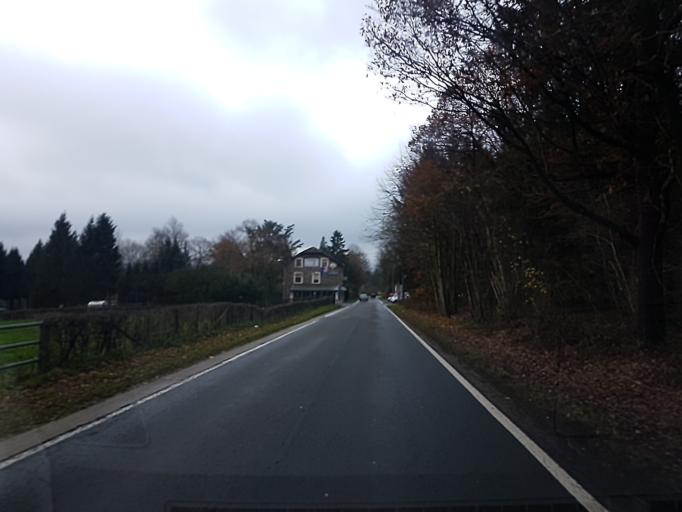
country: BE
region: Wallonia
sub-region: Province de Liege
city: Jalhay
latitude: 50.5752
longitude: 5.9682
